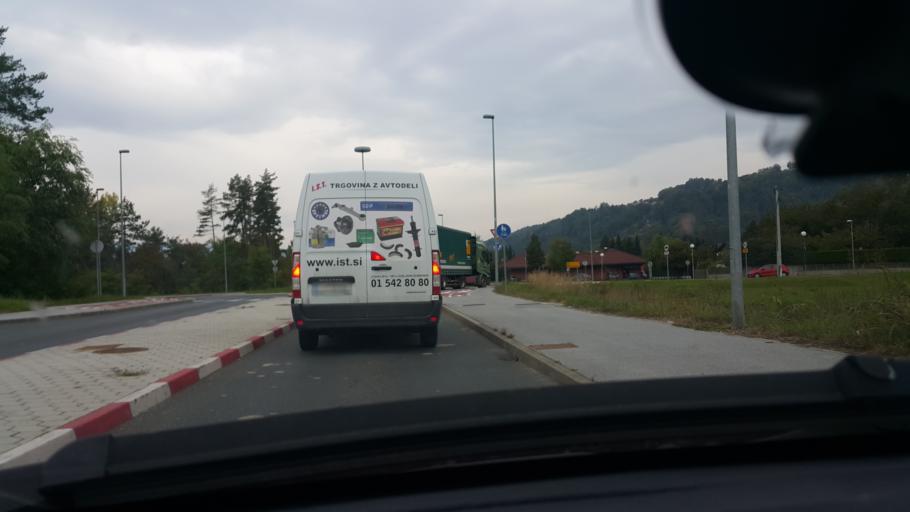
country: SI
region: Maribor
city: Bresternica
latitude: 46.5671
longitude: 15.5804
